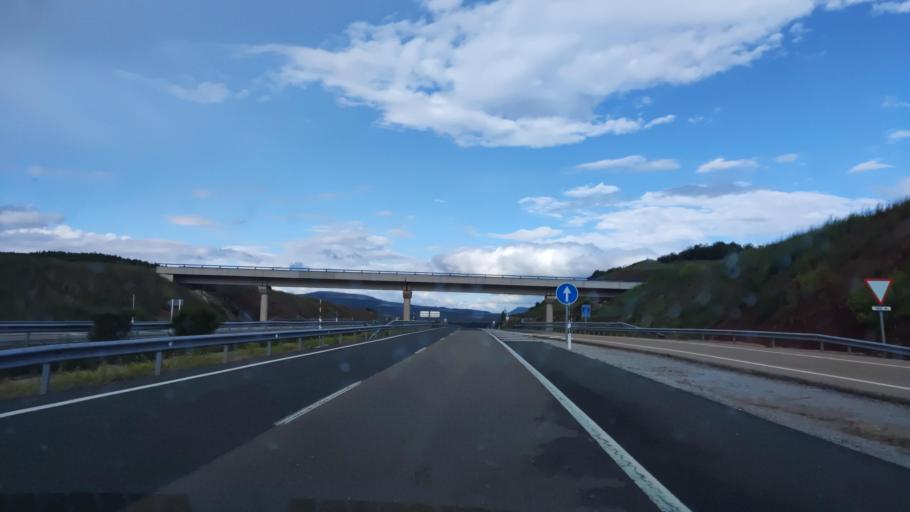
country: ES
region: Castille and Leon
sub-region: Provincia de Palencia
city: Aguilar de Campoo
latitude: 42.7705
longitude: -4.2684
